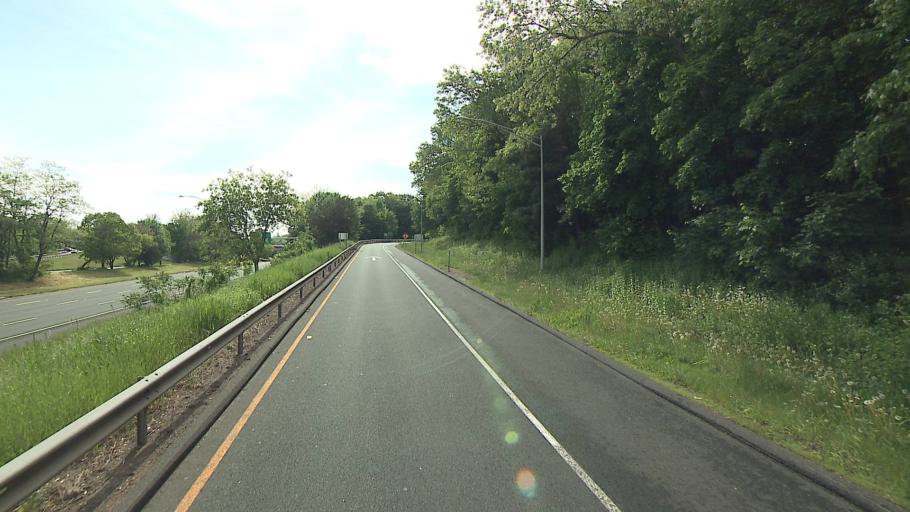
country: US
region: Connecticut
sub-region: Hartford County
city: Manchester
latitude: 41.7636
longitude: -72.5447
